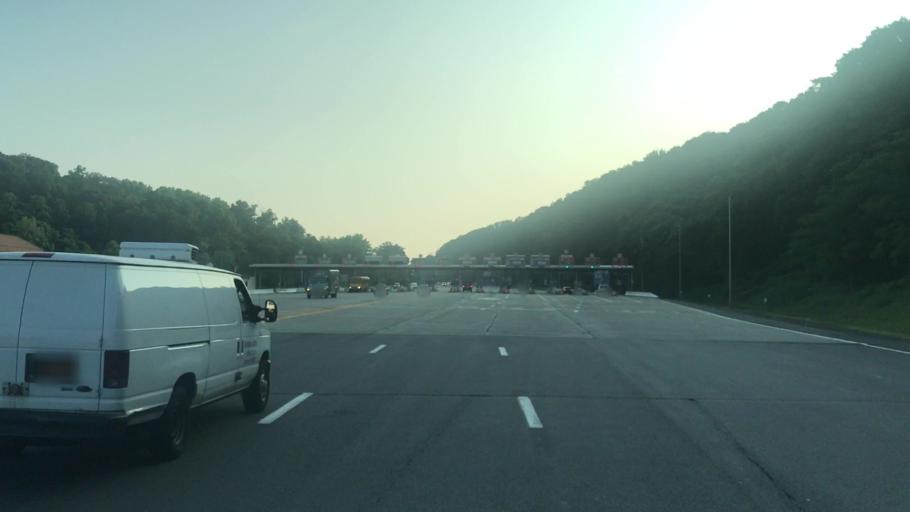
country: US
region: New York
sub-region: Westchester County
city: Hastings-on-Hudson
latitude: 40.9745
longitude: -73.8593
